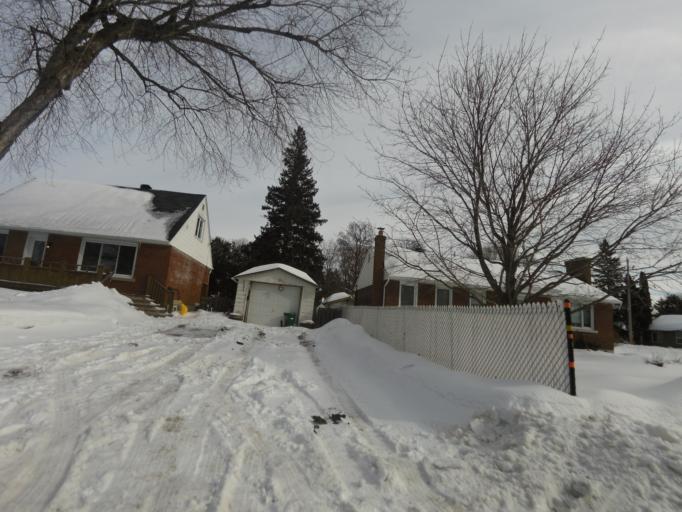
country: CA
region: Ontario
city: Ottawa
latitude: 45.4428
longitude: -75.6119
